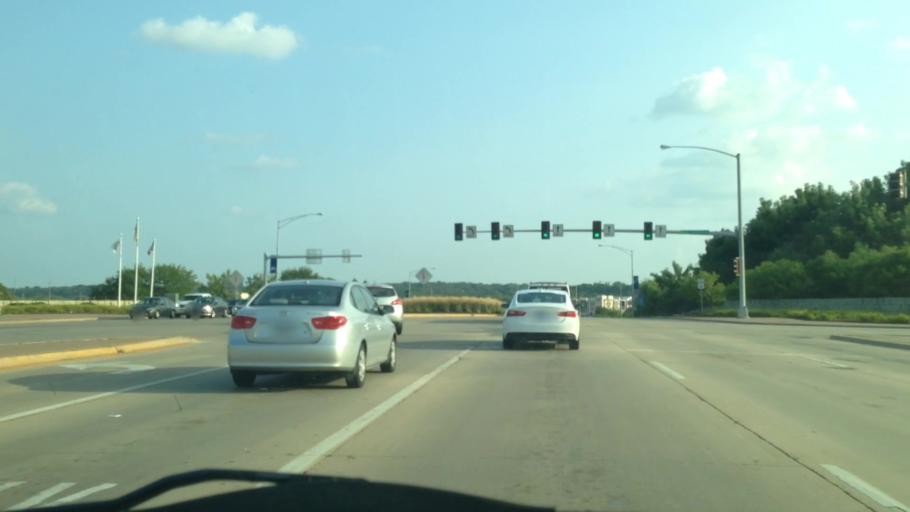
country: US
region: Iowa
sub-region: Johnson County
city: Coralville
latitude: 41.6925
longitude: -91.6086
